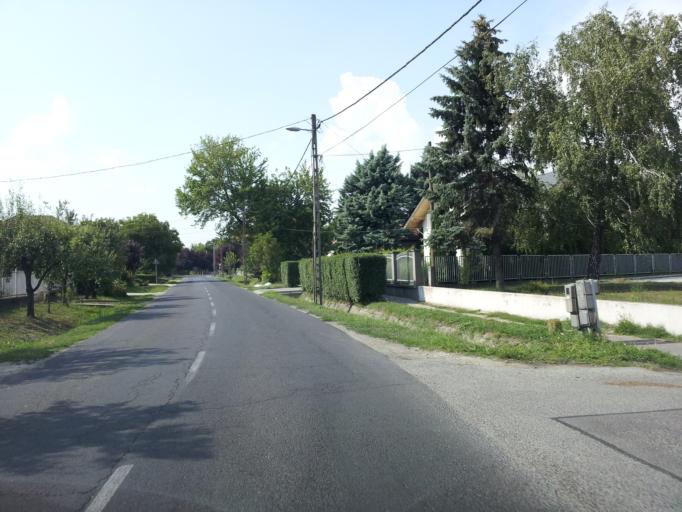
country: HU
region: Pest
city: Toekoel
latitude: 47.3192
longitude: 18.9623
